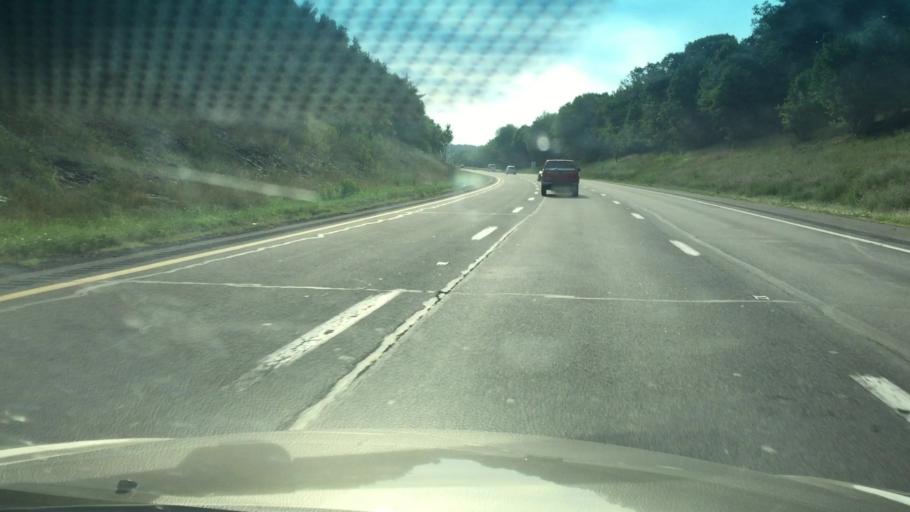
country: US
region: Pennsylvania
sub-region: Monroe County
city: Tannersville
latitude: 41.0617
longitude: -75.3317
